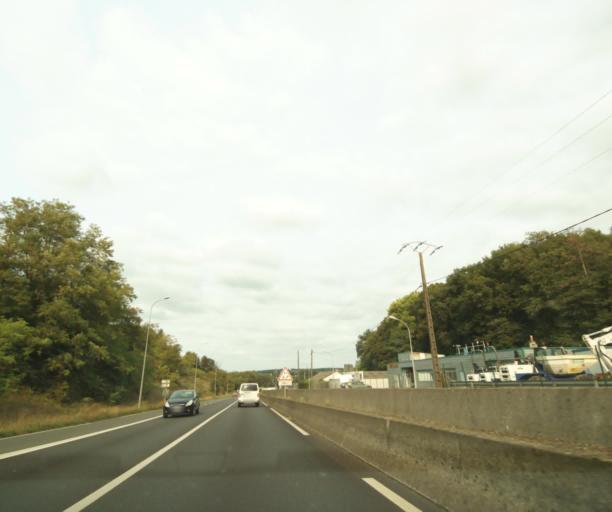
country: FR
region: Centre
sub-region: Departement d'Indre-et-Loire
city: Loches
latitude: 47.1392
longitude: 0.9964
